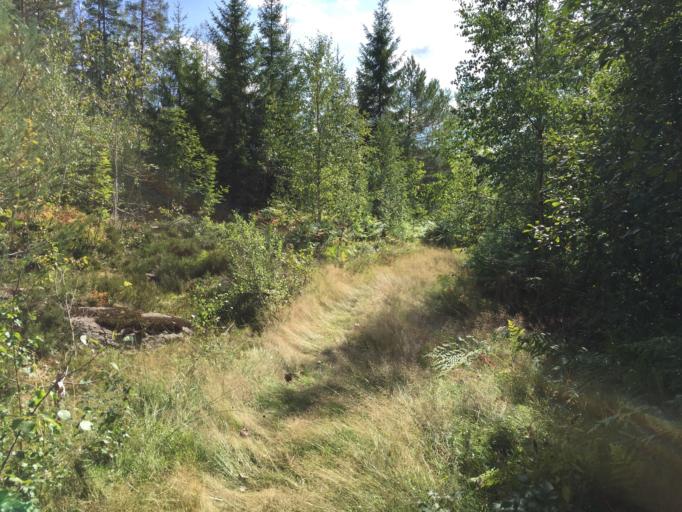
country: NO
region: Vestfold
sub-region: Hof
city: Hof
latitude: 59.4337
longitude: 10.1541
